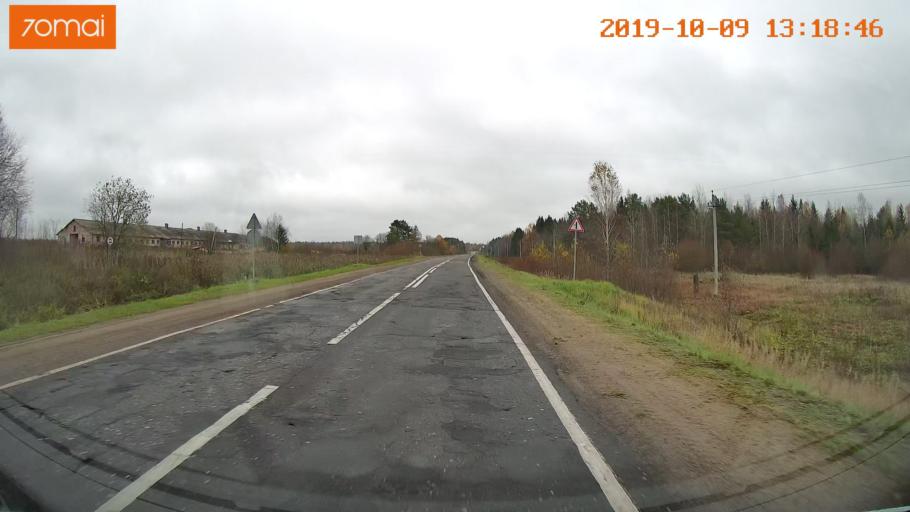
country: RU
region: Jaroslavl
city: Lyubim
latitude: 58.3503
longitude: 40.8007
